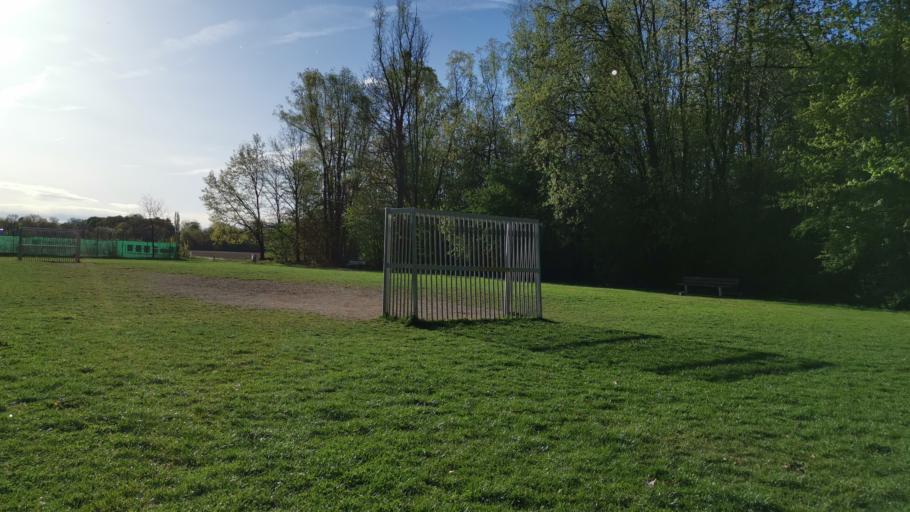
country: DE
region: Bavaria
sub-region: Upper Bavaria
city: Pullach im Isartal
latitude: 48.0883
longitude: 11.5223
